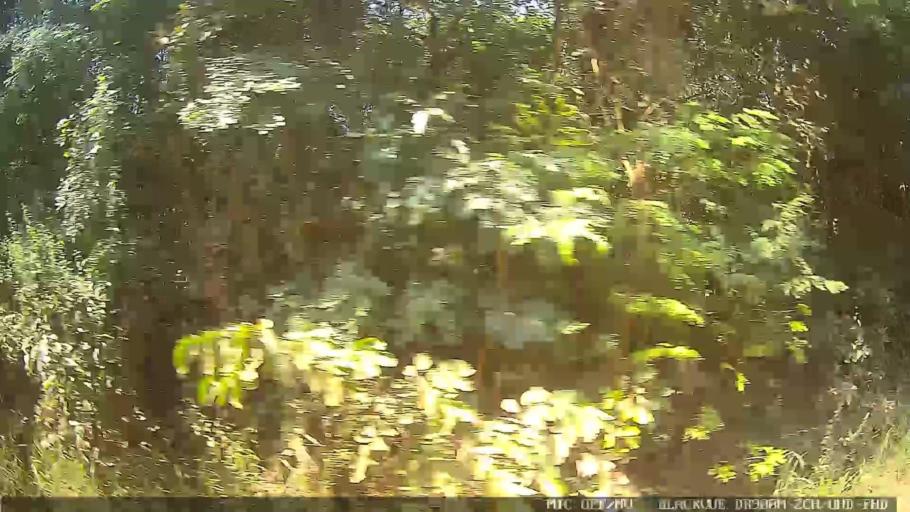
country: BR
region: Sao Paulo
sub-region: Jarinu
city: Jarinu
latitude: -23.0689
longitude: -46.6731
